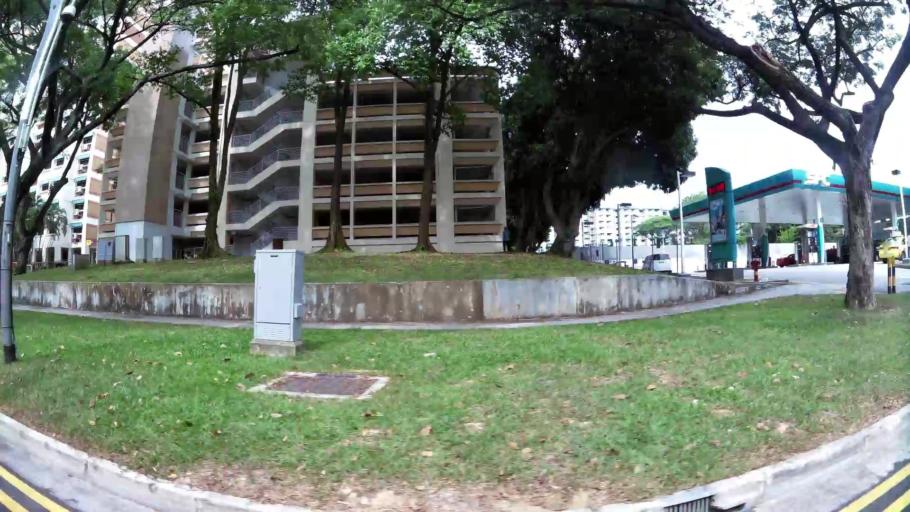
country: SG
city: Singapore
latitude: 1.3058
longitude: 103.7948
